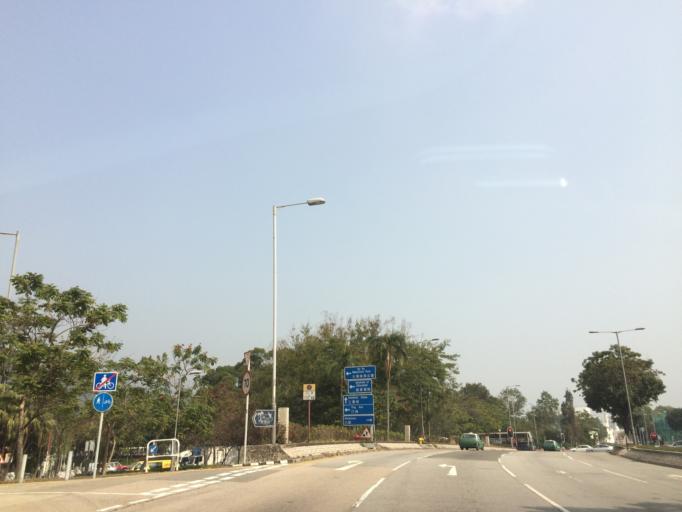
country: HK
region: Tai Po
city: Tai Po
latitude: 22.4566
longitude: 114.1763
